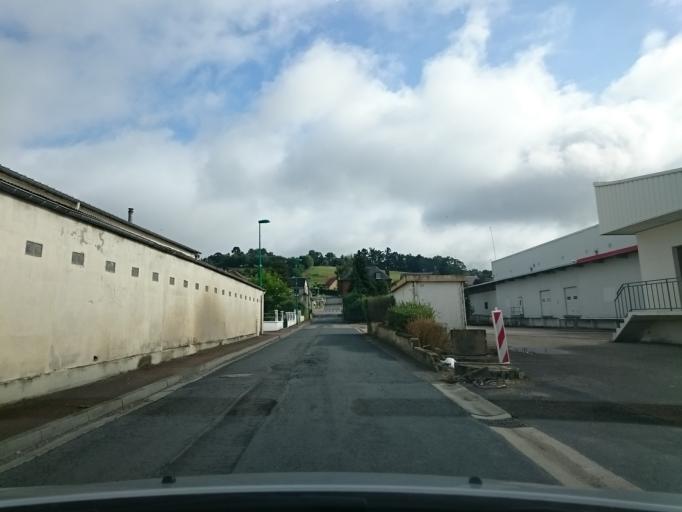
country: FR
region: Lower Normandy
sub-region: Departement du Calvados
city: Beuvillers
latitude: 49.1298
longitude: 0.2573
